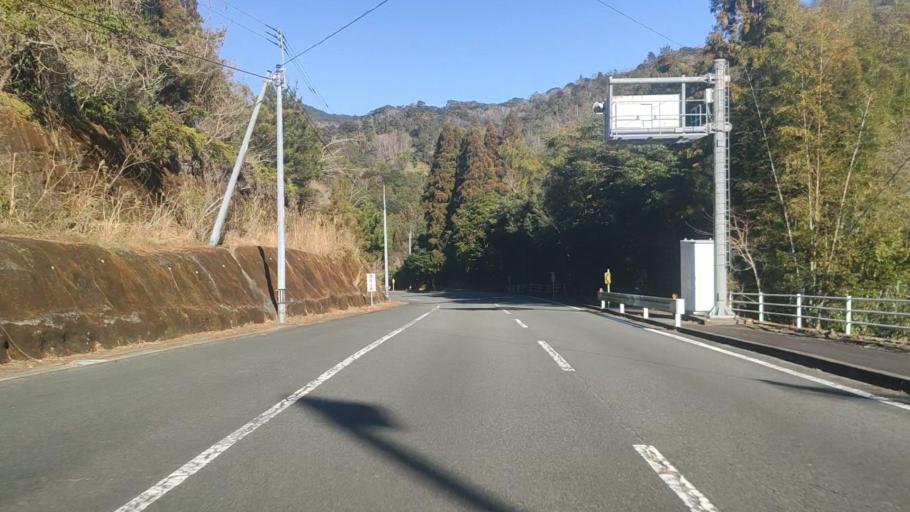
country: JP
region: Oita
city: Saiki
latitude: 32.7405
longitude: 131.8245
